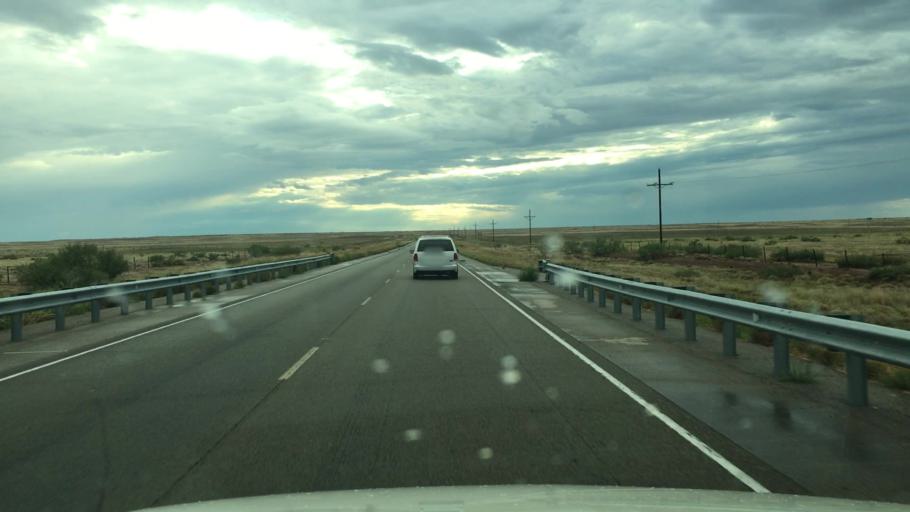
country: US
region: New Mexico
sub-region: Chaves County
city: Dexter
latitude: 33.4064
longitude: -104.3016
